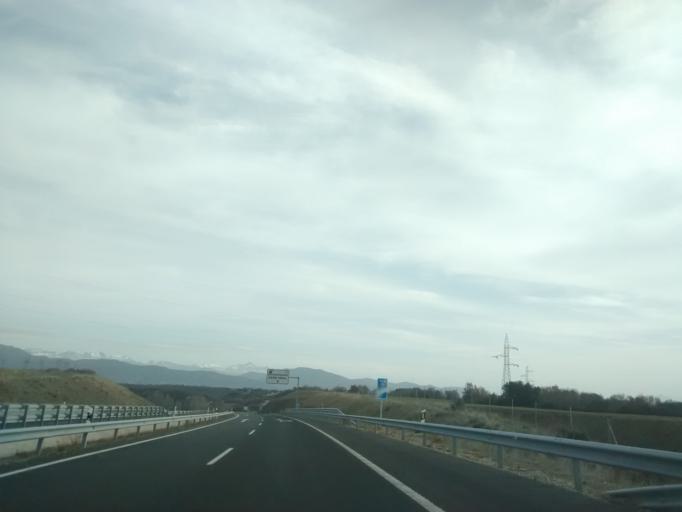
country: ES
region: Aragon
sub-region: Provincia de Zaragoza
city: Mianos
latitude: 42.6102
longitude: -0.9396
